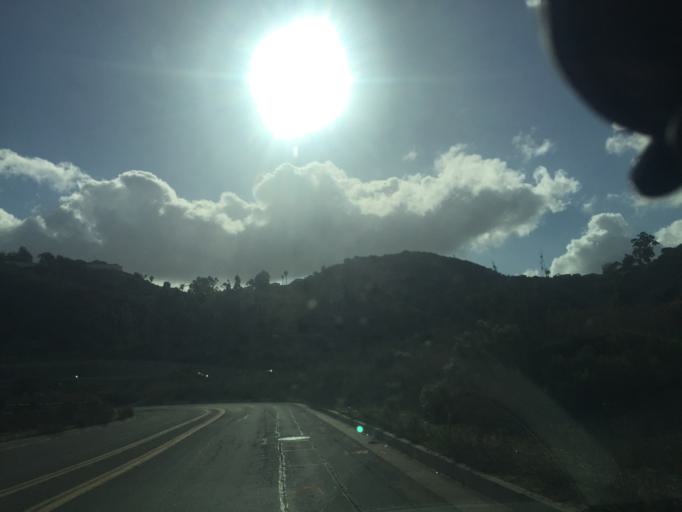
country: US
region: California
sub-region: San Diego County
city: San Diego
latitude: 32.7767
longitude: -117.1247
